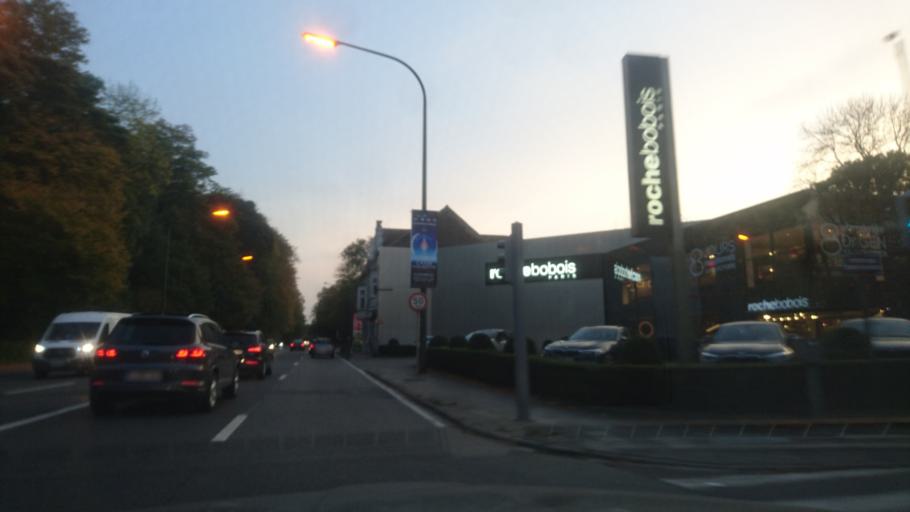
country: BE
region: Flanders
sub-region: Provincie Vlaams-Brabant
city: Sint-Genesius-Rode
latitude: 50.7694
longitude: 4.3827
